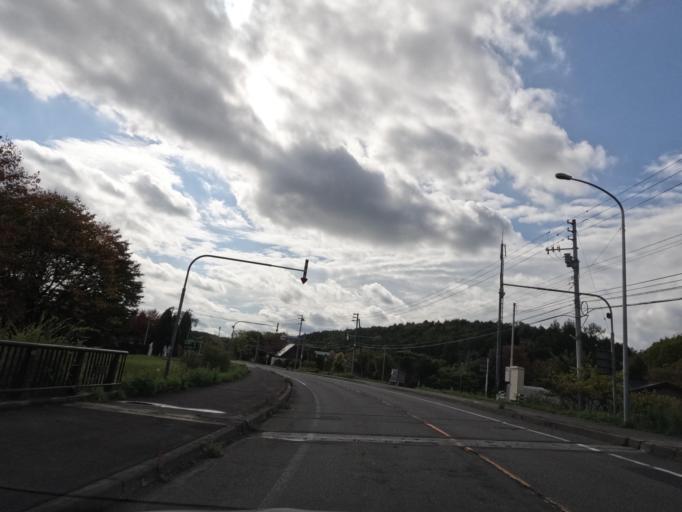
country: JP
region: Hokkaido
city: Chitose
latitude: 42.8160
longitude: 141.5951
